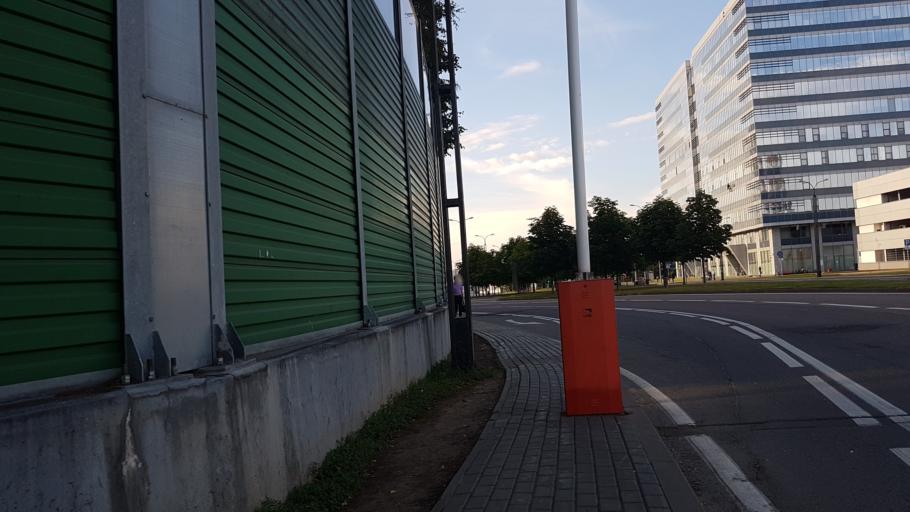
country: RU
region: Moscow
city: Strogino
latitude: 55.8133
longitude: 37.3840
